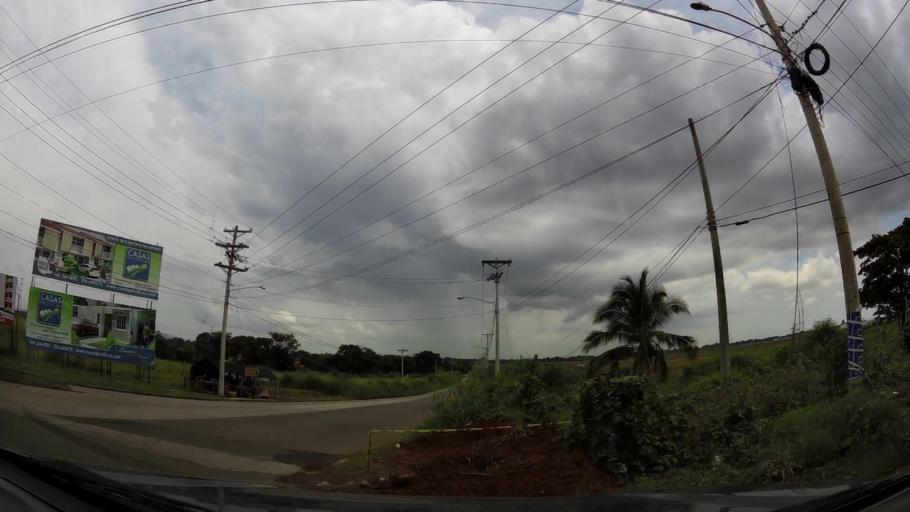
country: PA
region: Panama
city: Cabra Numero Uno
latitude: 9.1103
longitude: -79.3202
